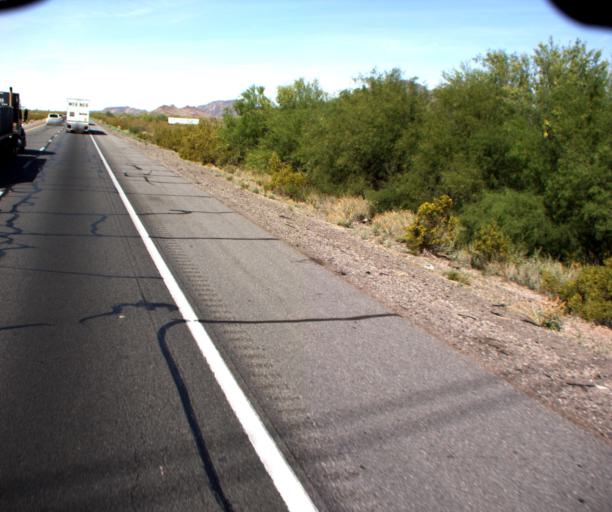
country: US
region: Arizona
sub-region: Maricopa County
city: Buckeye
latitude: 33.5144
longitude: -113.0314
